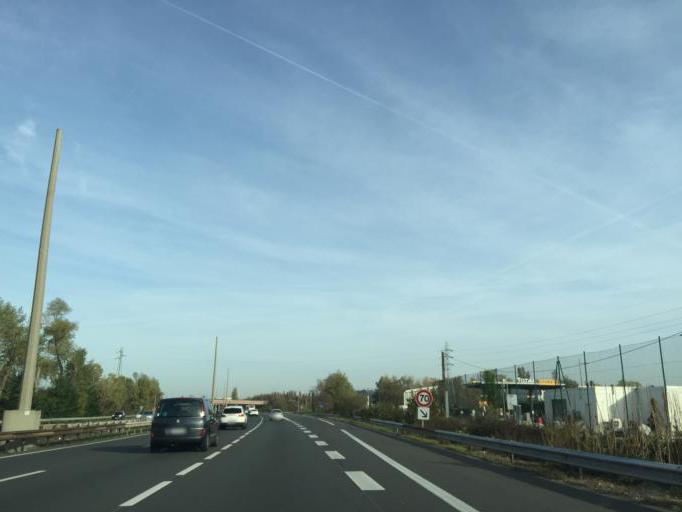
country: FR
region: Rhone-Alpes
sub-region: Departement du Rhone
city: Feyzin
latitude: 45.6742
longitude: 4.8479
